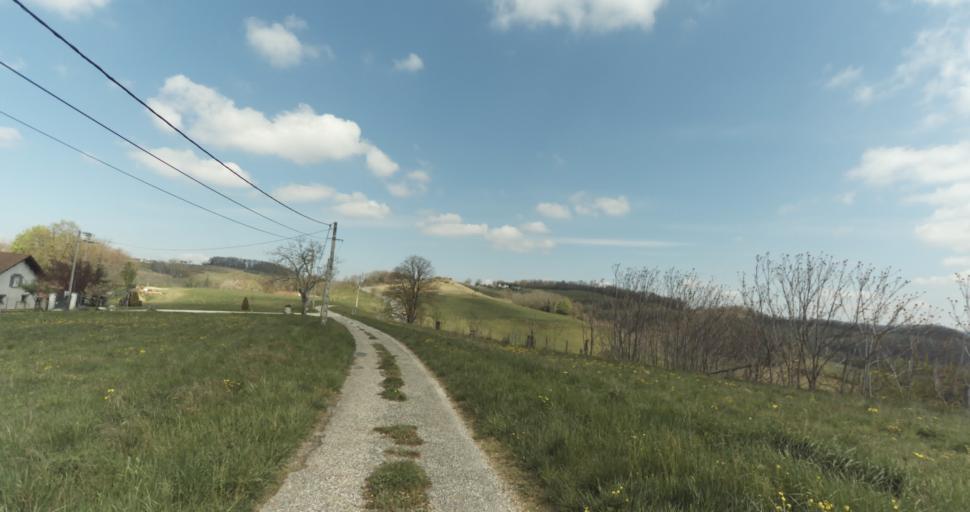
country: FR
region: Rhone-Alpes
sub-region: Departement de l'Isere
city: Saint-Verand
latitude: 45.1704
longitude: 5.3198
